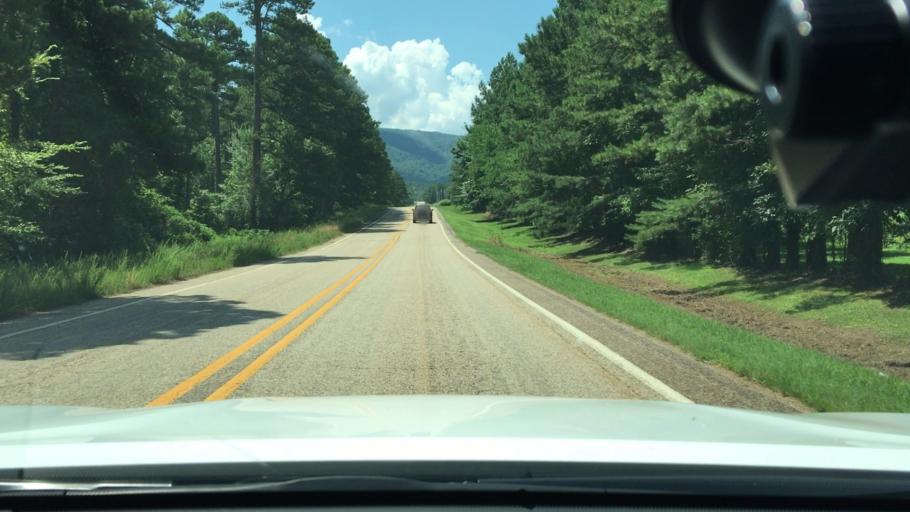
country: US
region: Arkansas
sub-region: Logan County
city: Paris
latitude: 35.2084
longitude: -93.6346
